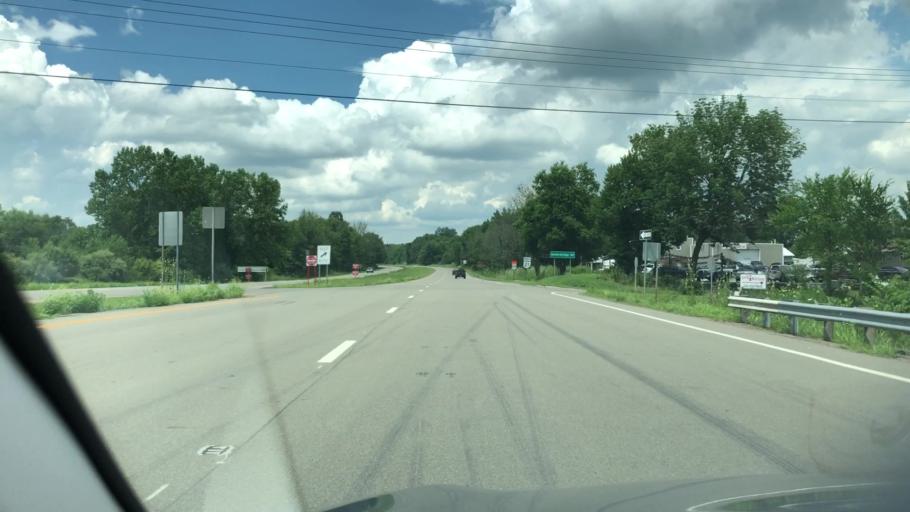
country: US
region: Ohio
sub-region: Stark County
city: Canal Fulton
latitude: 40.8573
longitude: -81.5788
